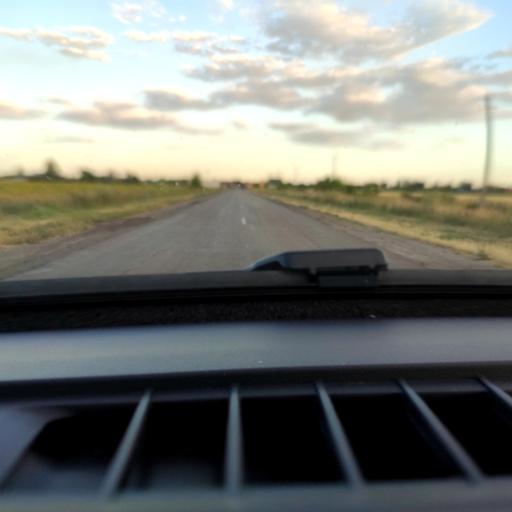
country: RU
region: Voronezj
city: Orlovo
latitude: 51.6710
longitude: 39.6876
